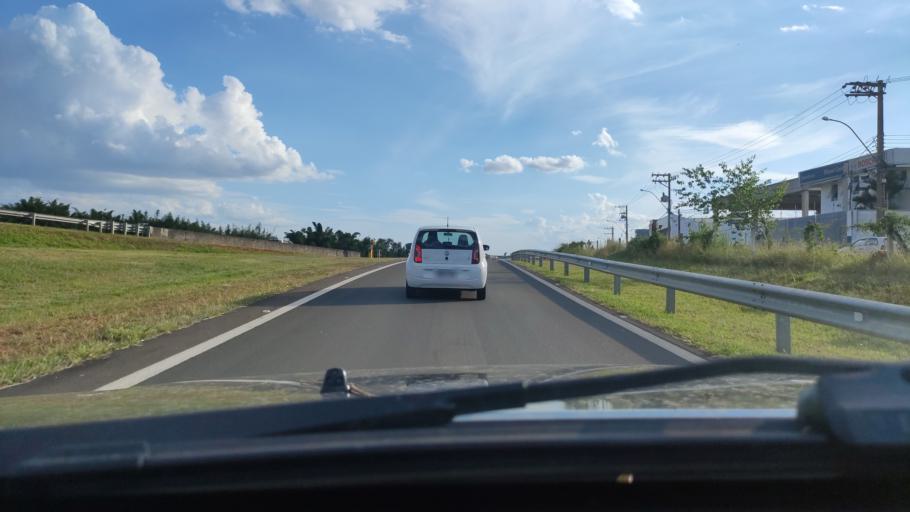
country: BR
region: Sao Paulo
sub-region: Itapira
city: Itapira
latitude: -22.4466
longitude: -46.8332
